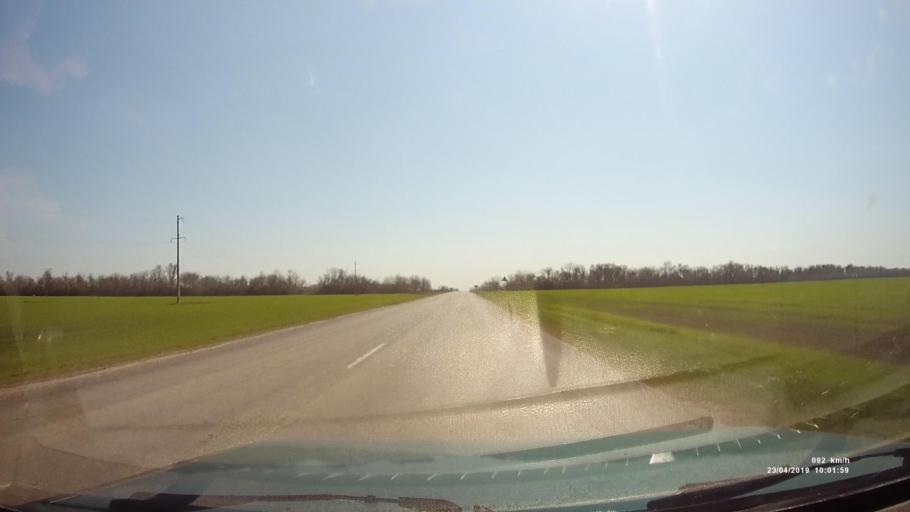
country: RU
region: Rostov
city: Sovetskoye
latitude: 46.7625
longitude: 42.1590
